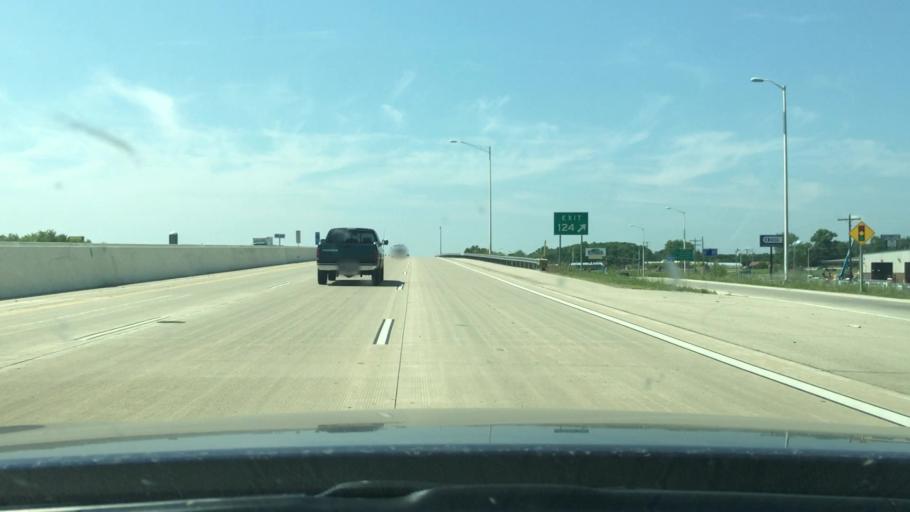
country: US
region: Wisconsin
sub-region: Winnebago County
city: Oshkosh
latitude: 44.0993
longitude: -88.5401
